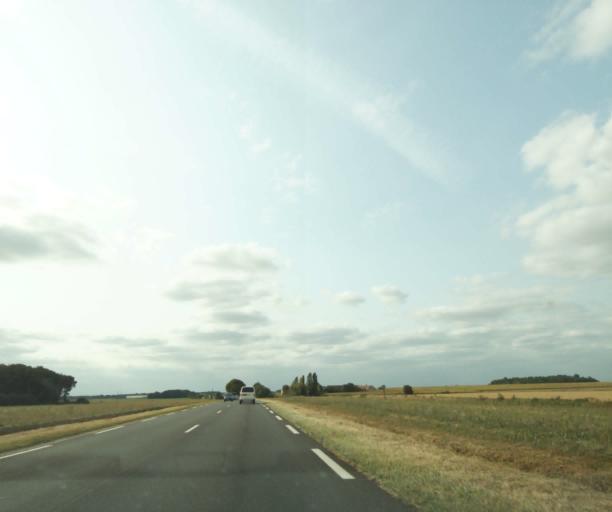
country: FR
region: Centre
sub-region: Departement d'Indre-et-Loire
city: Truyes
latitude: 47.2422
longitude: 0.8611
